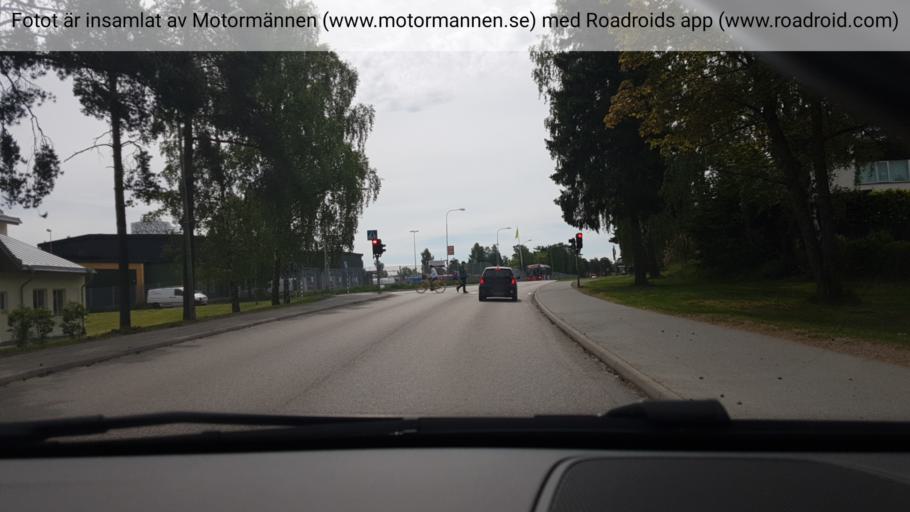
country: SE
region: Stockholm
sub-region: Haninge Kommun
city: Haninge
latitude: 59.1721
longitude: 18.1474
